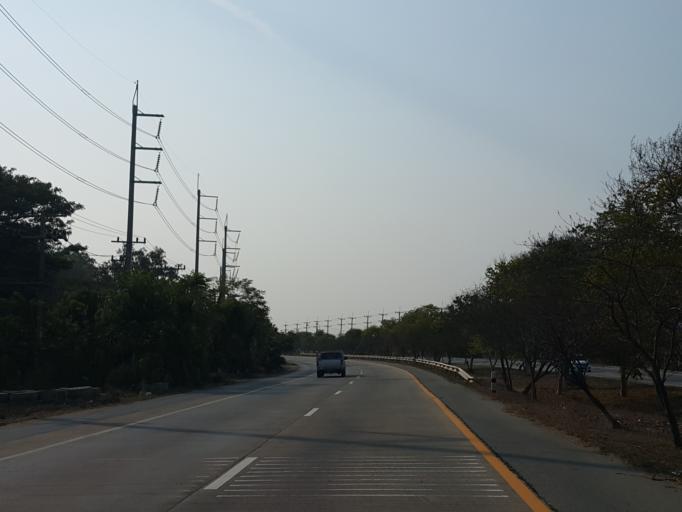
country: TH
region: Suphan Buri
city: Doembang Nangbuat
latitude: 14.8399
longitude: 100.1073
